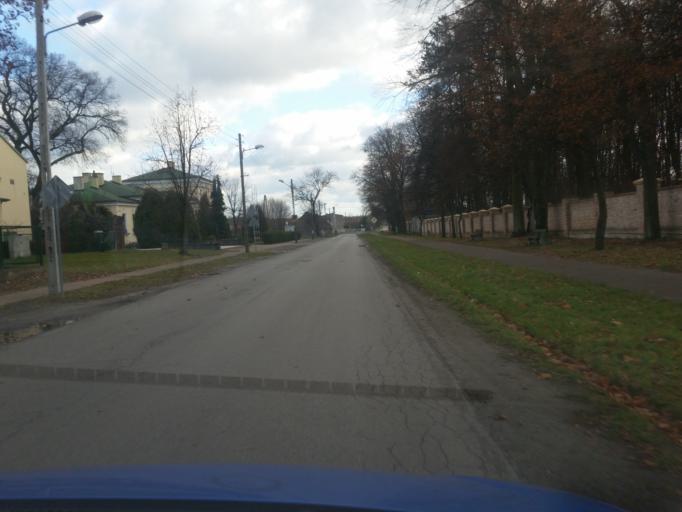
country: PL
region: Silesian Voivodeship
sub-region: Powiat czestochowski
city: Borowno
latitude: 50.9670
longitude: 19.2787
